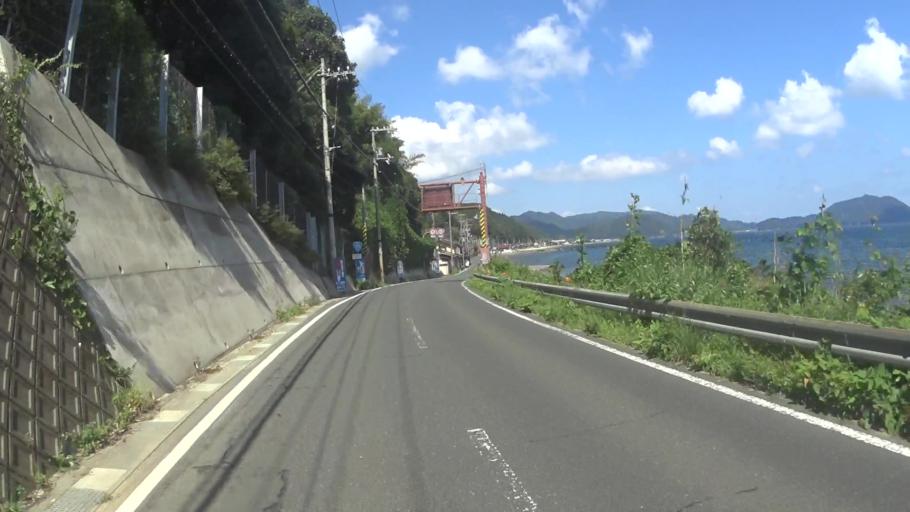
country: JP
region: Kyoto
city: Miyazu
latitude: 35.6451
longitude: 135.2510
